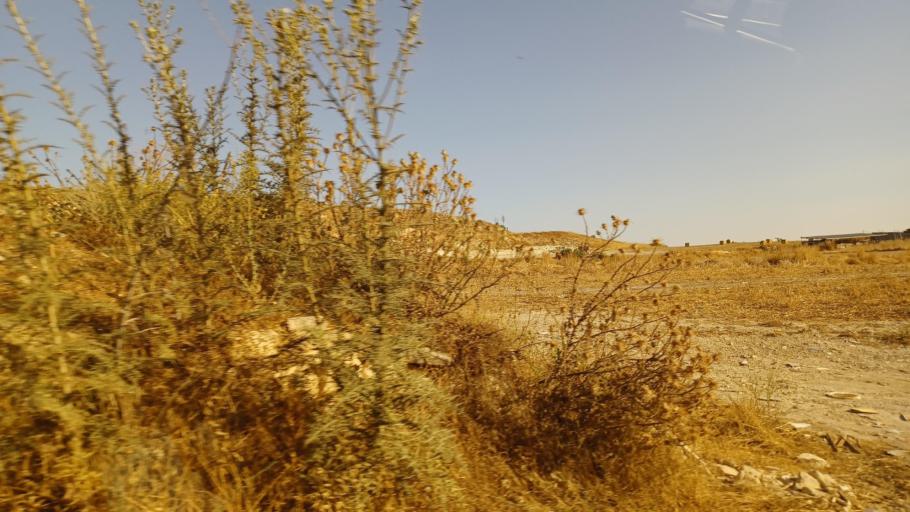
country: CY
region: Larnaka
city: Athienou
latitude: 35.0361
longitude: 33.5285
